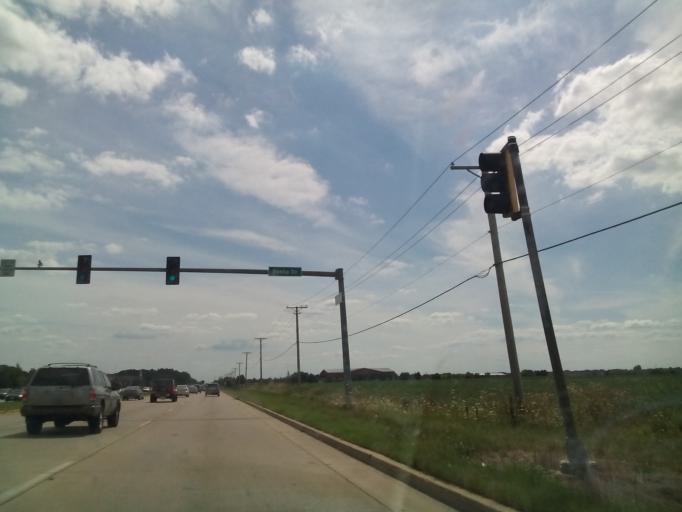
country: US
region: Illinois
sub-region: DuPage County
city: Naperville
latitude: 41.7446
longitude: -88.2061
